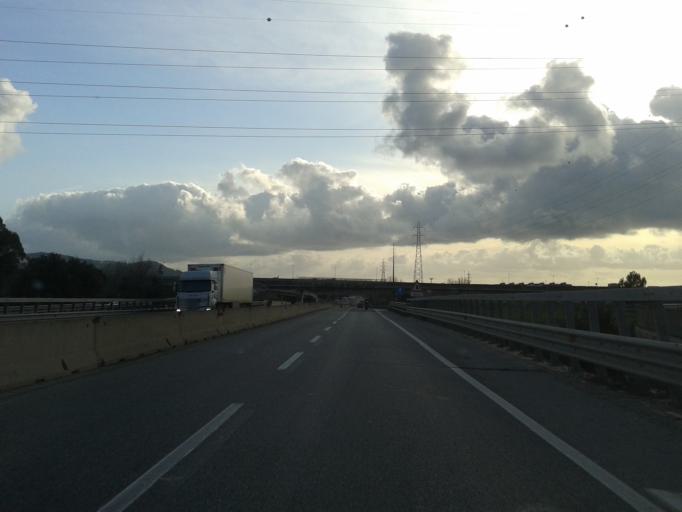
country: IT
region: Tuscany
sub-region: Provincia di Livorno
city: Livorno
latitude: 43.5347
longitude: 10.3343
